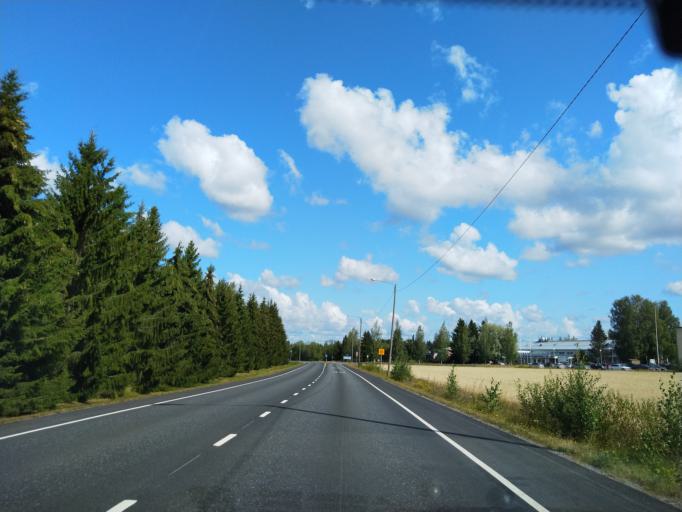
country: FI
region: Satakunta
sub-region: Pori
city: Huittinen
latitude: 61.1776
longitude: 22.7124
